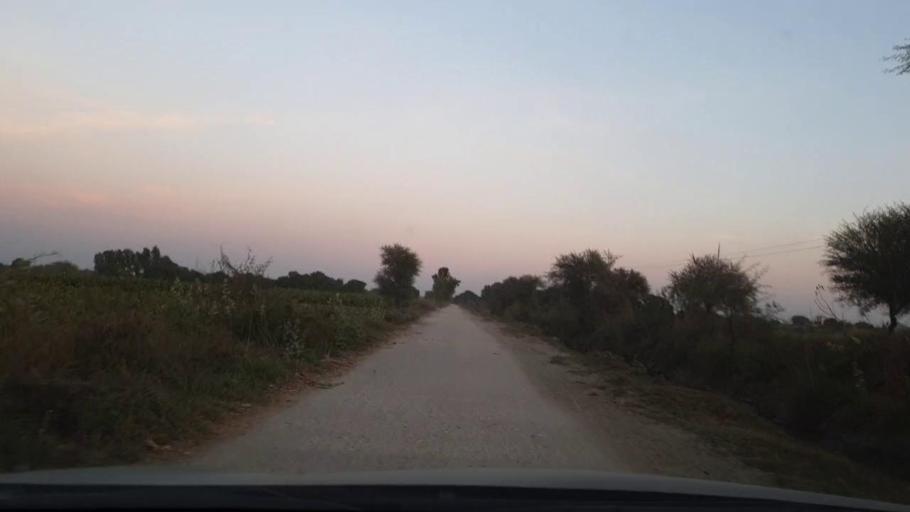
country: PK
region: Sindh
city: Tando Allahyar
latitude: 25.5564
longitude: 68.7838
